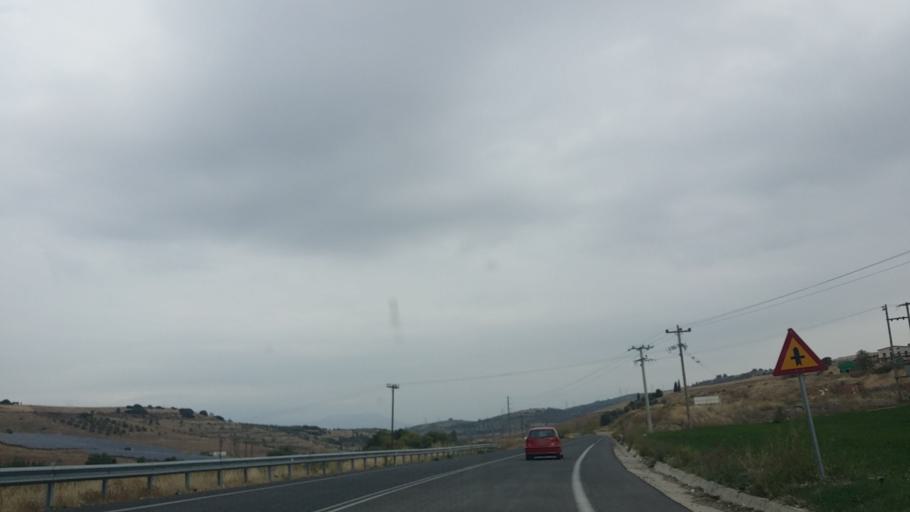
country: GR
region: Central Greece
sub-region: Nomos Voiotias
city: Vagia
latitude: 38.3028
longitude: 23.2386
